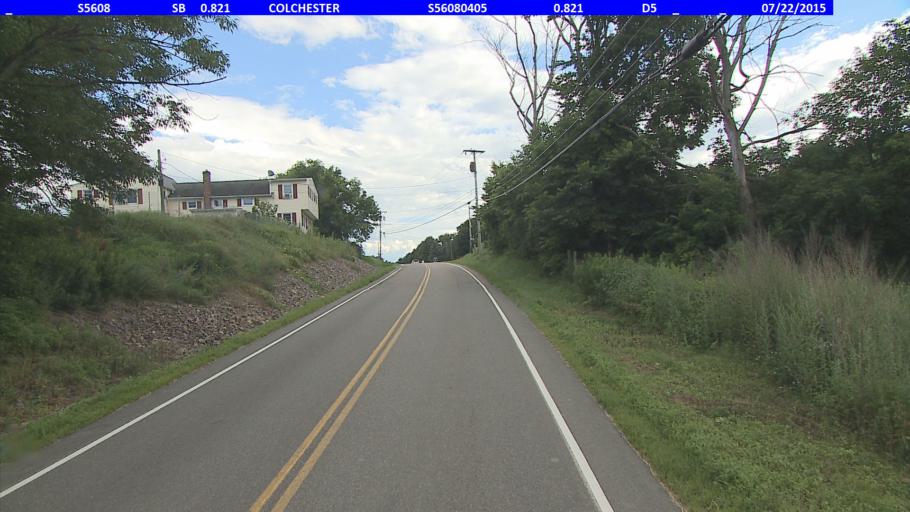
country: US
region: Vermont
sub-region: Chittenden County
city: Winooski
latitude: 44.5107
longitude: -73.2027
